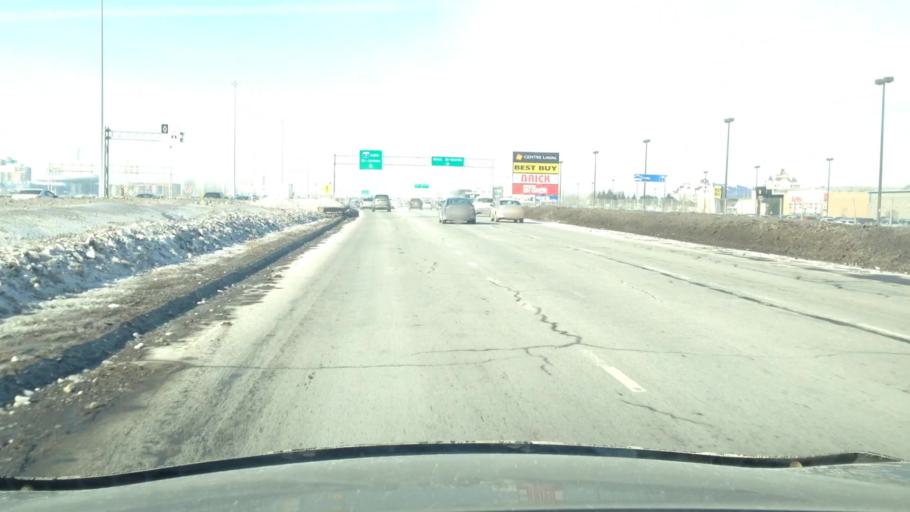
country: CA
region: Quebec
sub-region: Laval
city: Laval
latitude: 45.5584
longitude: -73.7319
